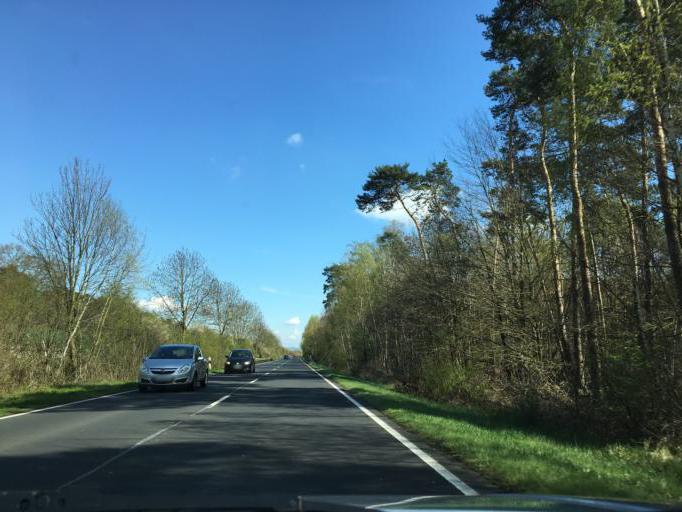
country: DE
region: Hesse
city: Obertshausen
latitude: 50.0607
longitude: 8.8573
